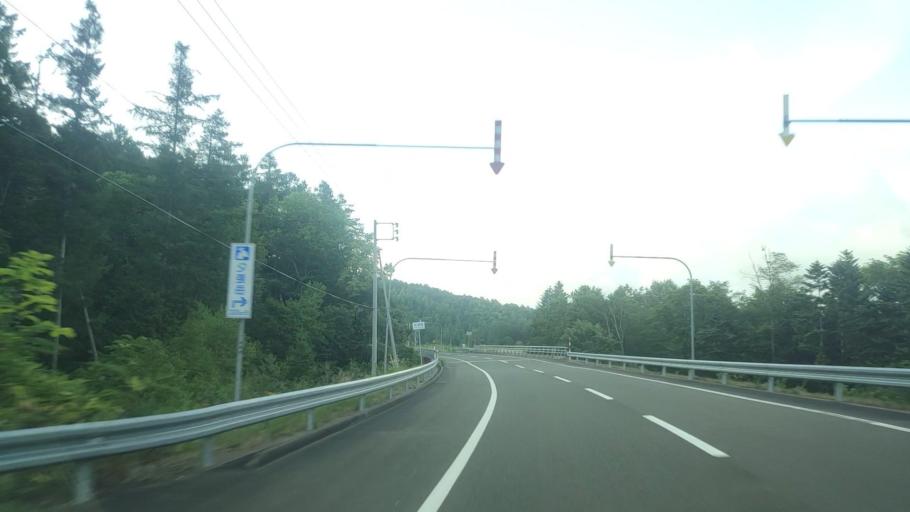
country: JP
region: Hokkaido
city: Bibai
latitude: 43.0603
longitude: 142.0995
